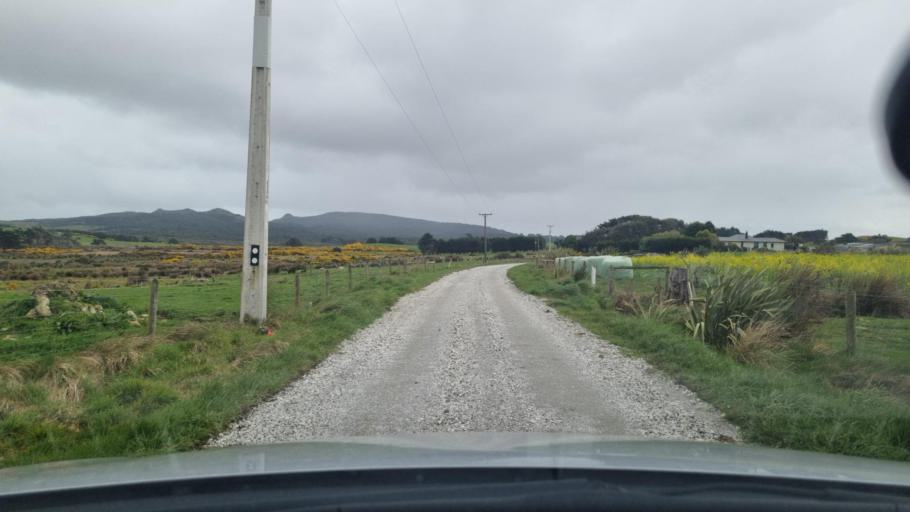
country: NZ
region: Southland
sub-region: Invercargill City
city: Bluff
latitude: -46.5441
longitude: 168.2967
